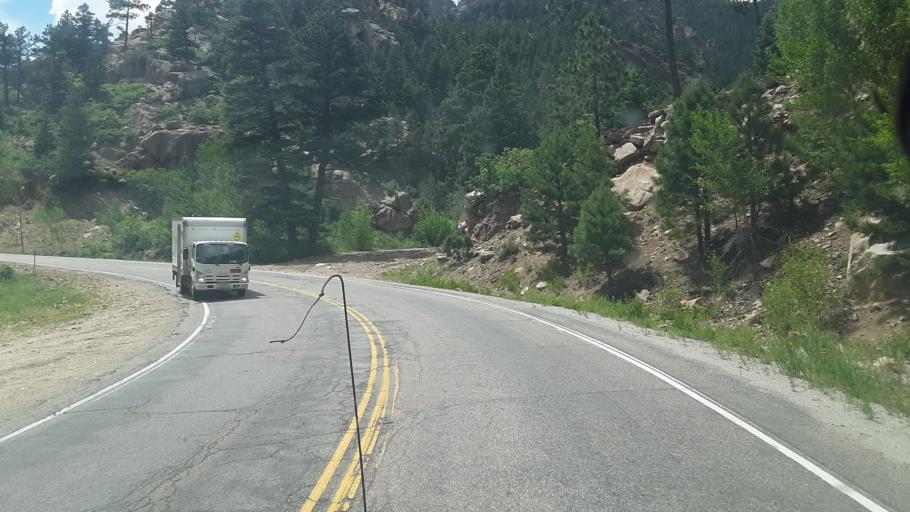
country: US
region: Colorado
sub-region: Fremont County
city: Florence
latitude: 38.1747
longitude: -105.1677
